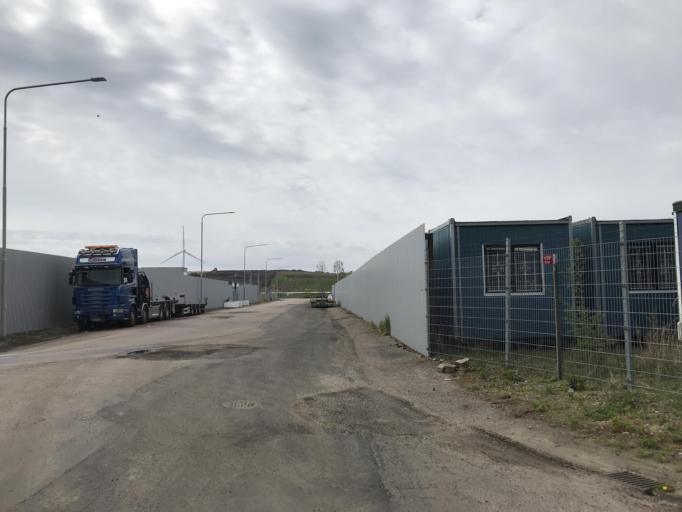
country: SE
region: Skane
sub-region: Landskrona
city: Landskrona
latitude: 55.8669
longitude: 12.8632
